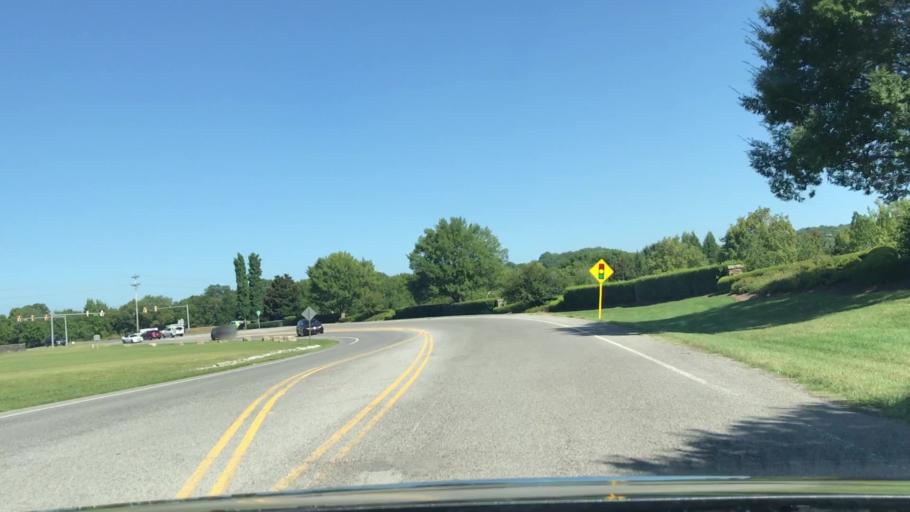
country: US
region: Tennessee
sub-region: Williamson County
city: Franklin
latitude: 35.9789
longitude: -86.8867
